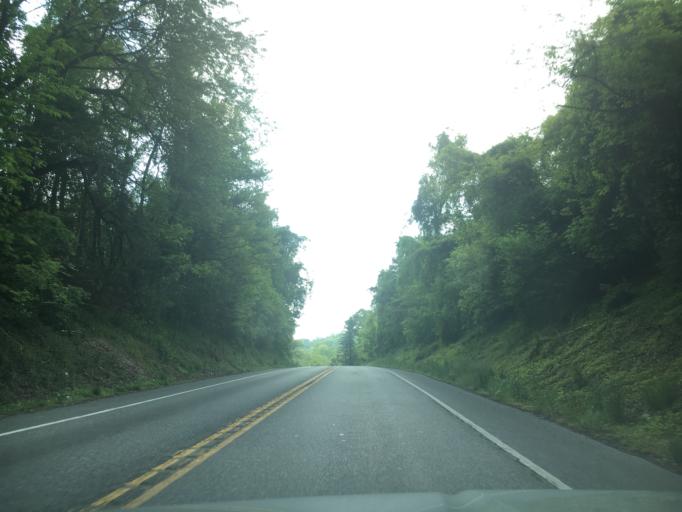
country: US
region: Pennsylvania
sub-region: Berks County
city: New Berlinville
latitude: 40.3623
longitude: -75.6928
